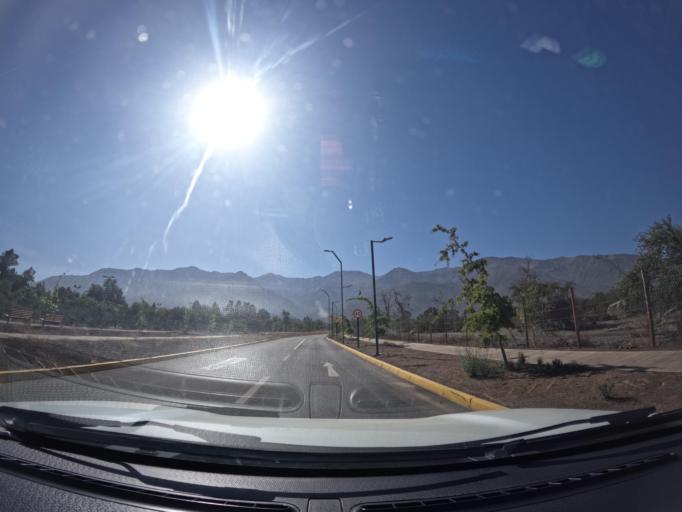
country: CL
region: Santiago Metropolitan
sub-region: Provincia de Santiago
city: Villa Presidente Frei, Nunoa, Santiago, Chile
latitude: -33.5020
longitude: -70.5372
